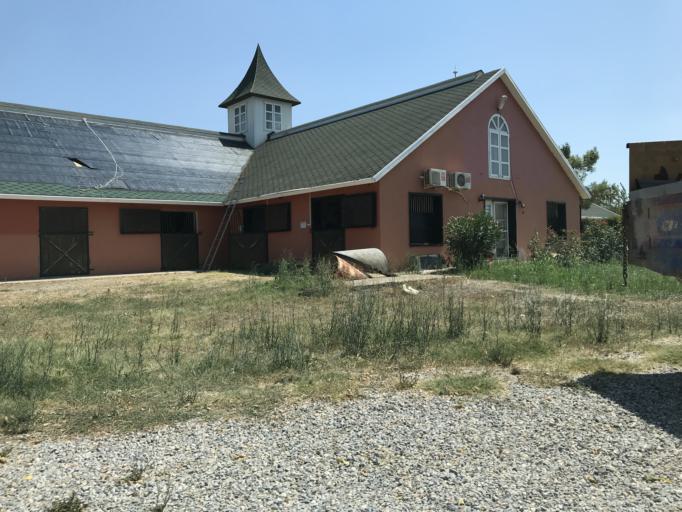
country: TR
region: Izmir
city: Urla
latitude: 38.2890
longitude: 26.7229
